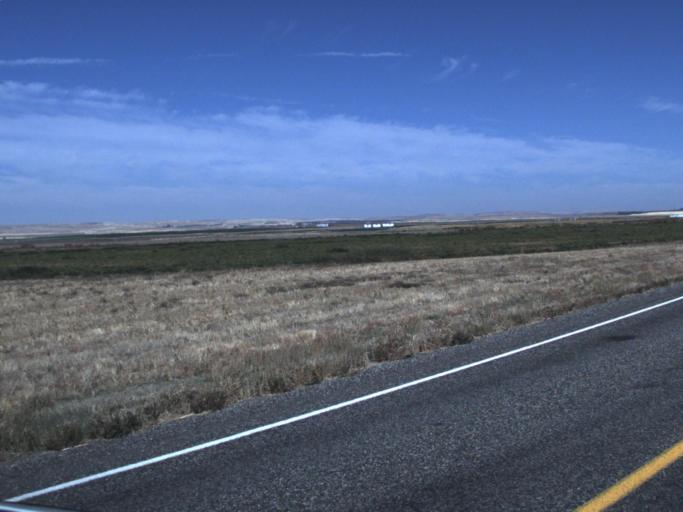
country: US
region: Washington
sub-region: Walla Walla County
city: Burbank
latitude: 46.2509
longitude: -118.8091
